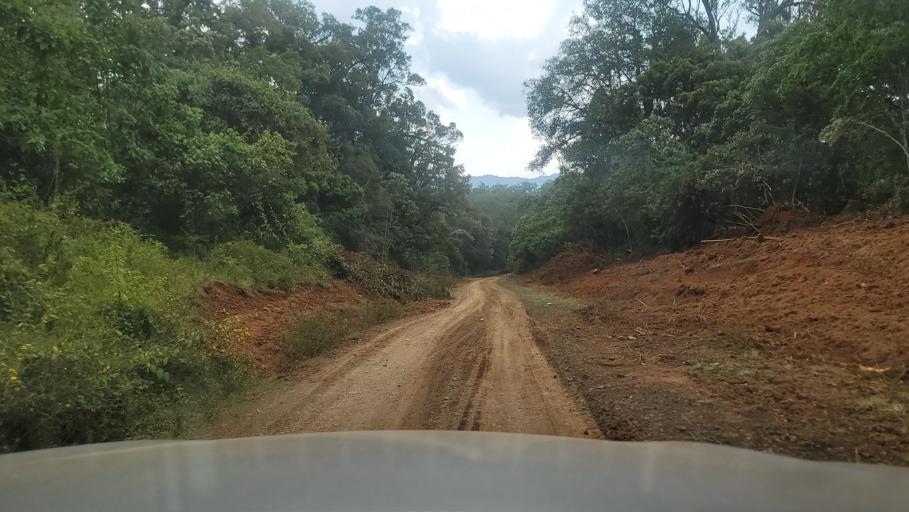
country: ET
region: Southern Nations, Nationalities, and People's Region
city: Bonga
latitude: 7.6628
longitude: 36.2460
